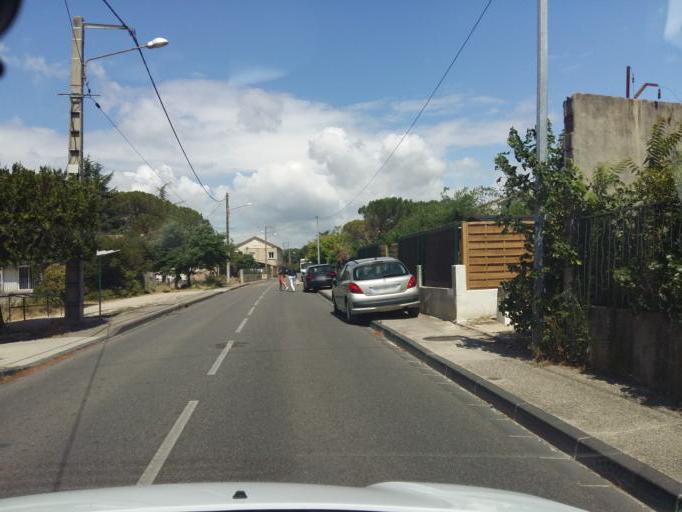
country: FR
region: Provence-Alpes-Cote d'Azur
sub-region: Departement du Vaucluse
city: Vaison-la-Romaine
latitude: 44.2468
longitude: 5.0685
